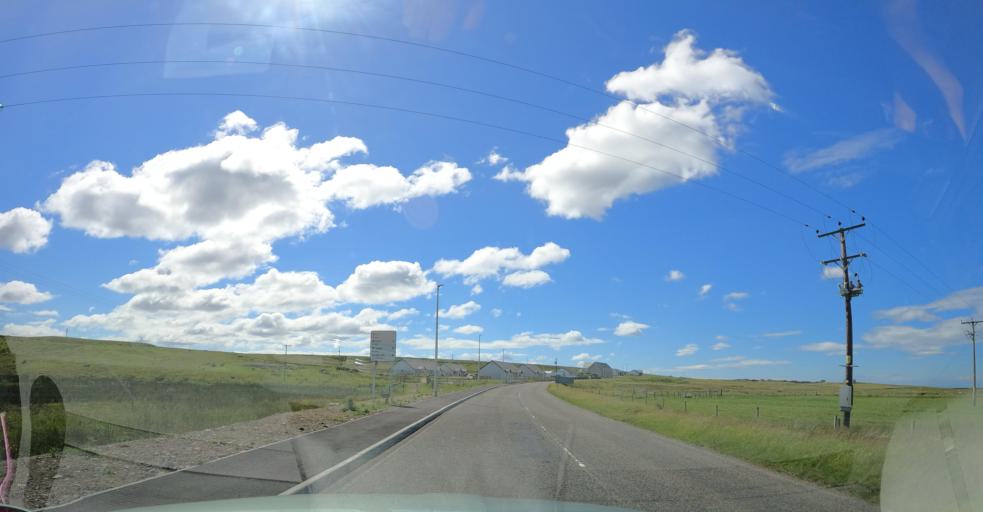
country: GB
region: Scotland
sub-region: Eilean Siar
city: Isle of Lewis
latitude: 58.3487
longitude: -6.5210
